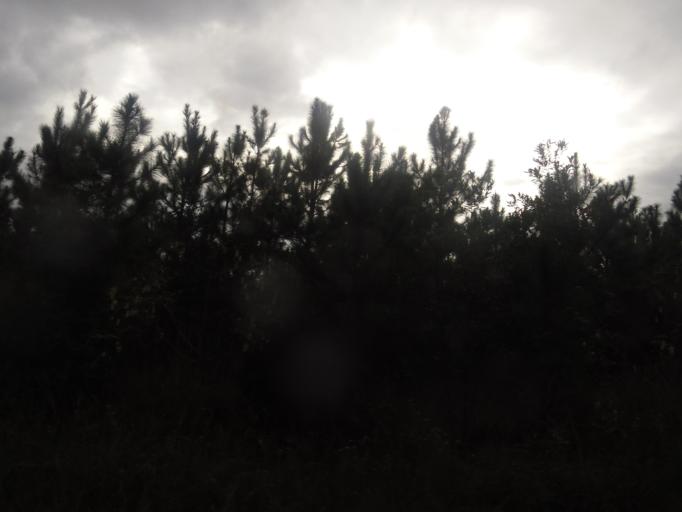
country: US
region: Florida
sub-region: Flagler County
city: Bunnell
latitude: 29.5469
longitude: -81.3257
